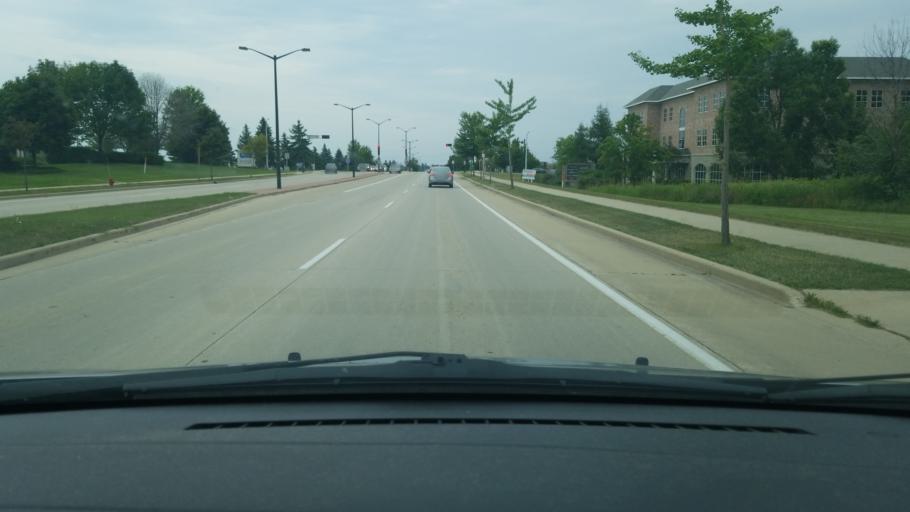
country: US
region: Wisconsin
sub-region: Ozaukee County
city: Grafton
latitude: 43.3202
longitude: -87.9370
